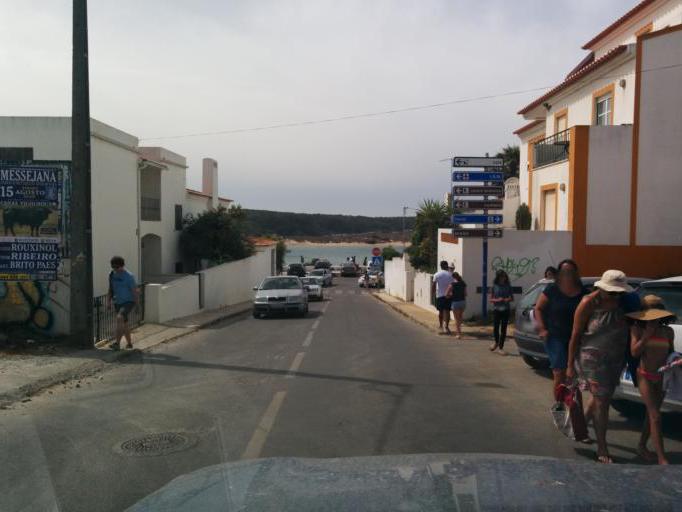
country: PT
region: Beja
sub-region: Odemira
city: Vila Nova de Milfontes
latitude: 37.7241
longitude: -8.7852
